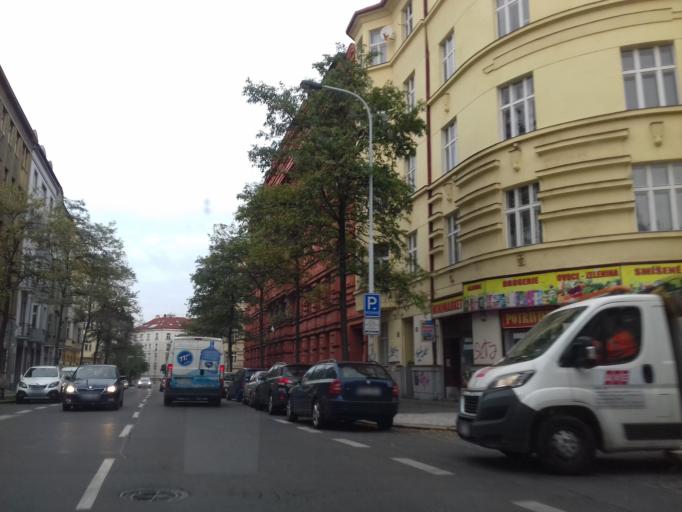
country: CZ
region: Praha
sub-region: Praha 8
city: Karlin
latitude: 50.0800
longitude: 14.4474
